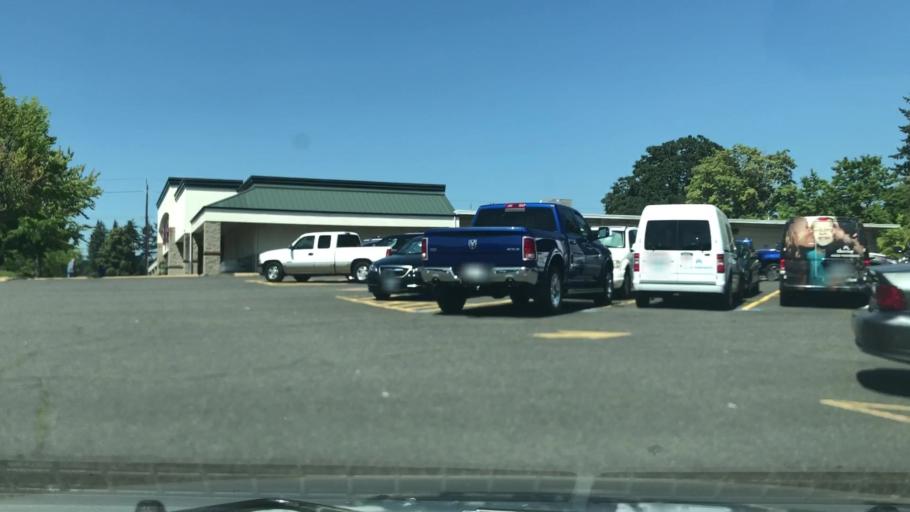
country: US
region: Oregon
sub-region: Washington County
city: Raleigh Hills
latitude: 45.4849
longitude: -122.7815
